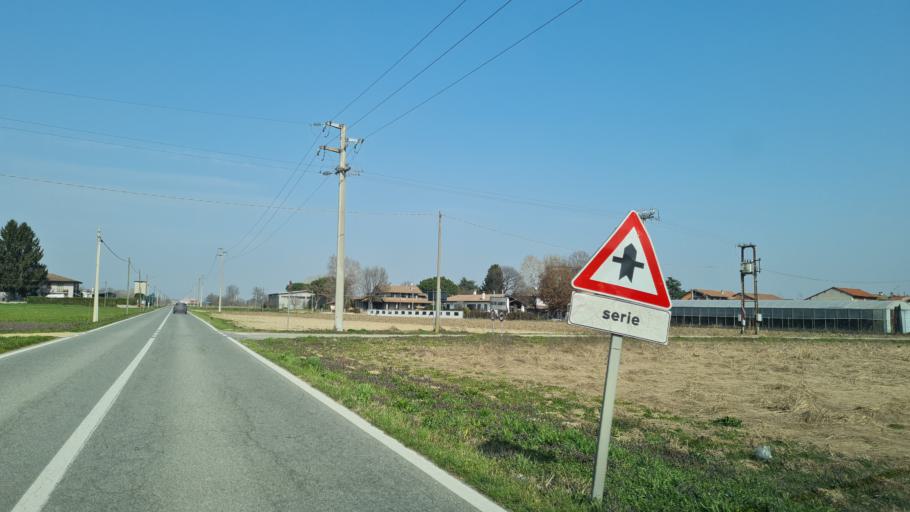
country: IT
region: Piedmont
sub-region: Provincia di Novara
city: Carpignano Sesia
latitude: 45.5155
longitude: 8.4196
